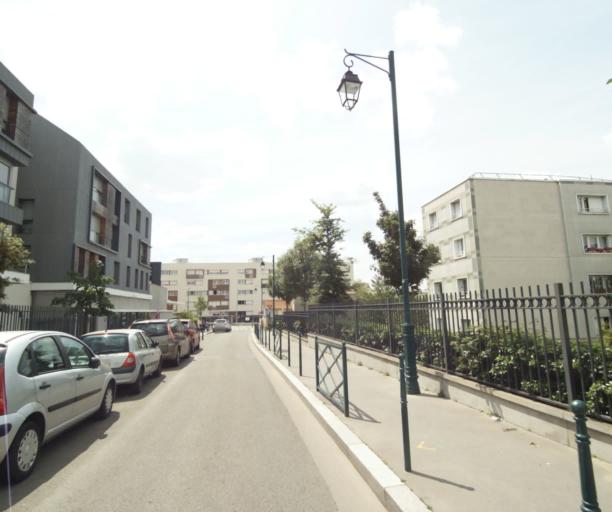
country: FR
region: Ile-de-France
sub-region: Departement du Val-d'Oise
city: Bezons
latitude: 48.9189
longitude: 2.2283
